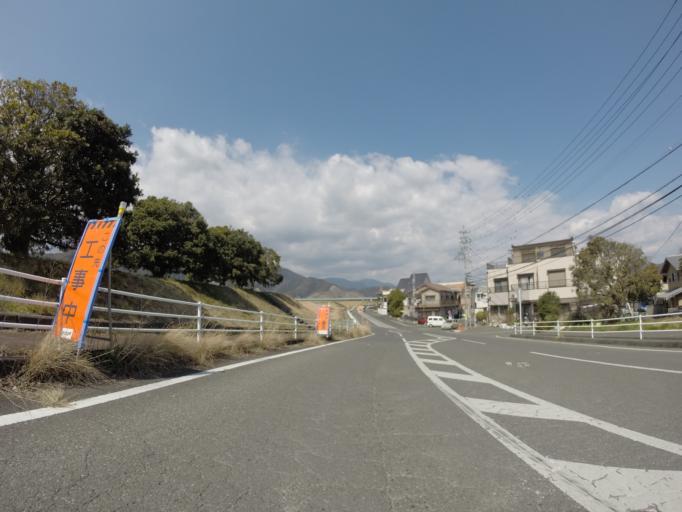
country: JP
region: Shizuoka
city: Shizuoka-shi
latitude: 34.9872
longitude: 138.3644
